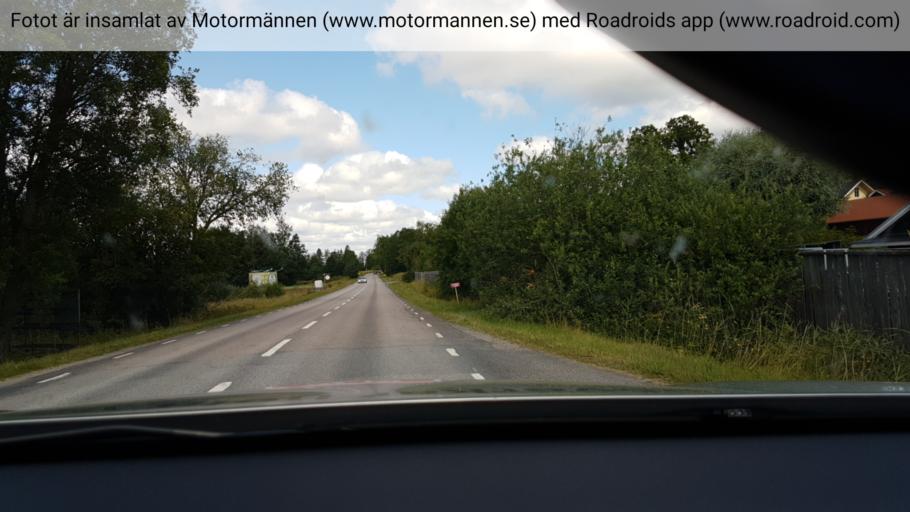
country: SE
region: Stockholm
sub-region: Norrtalje Kommun
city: Hallstavik
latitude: 59.9792
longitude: 18.8158
